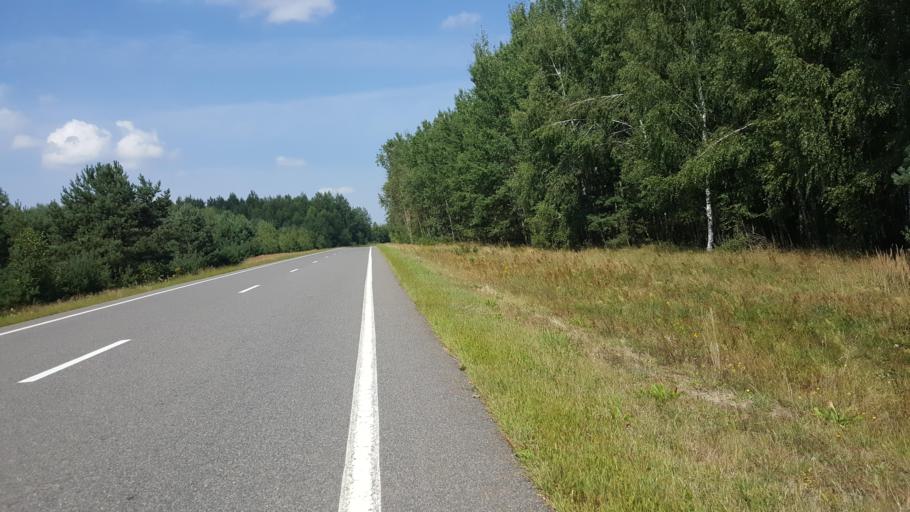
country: BY
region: Brest
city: Kamyanyuki
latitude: 52.5521
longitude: 23.6426
